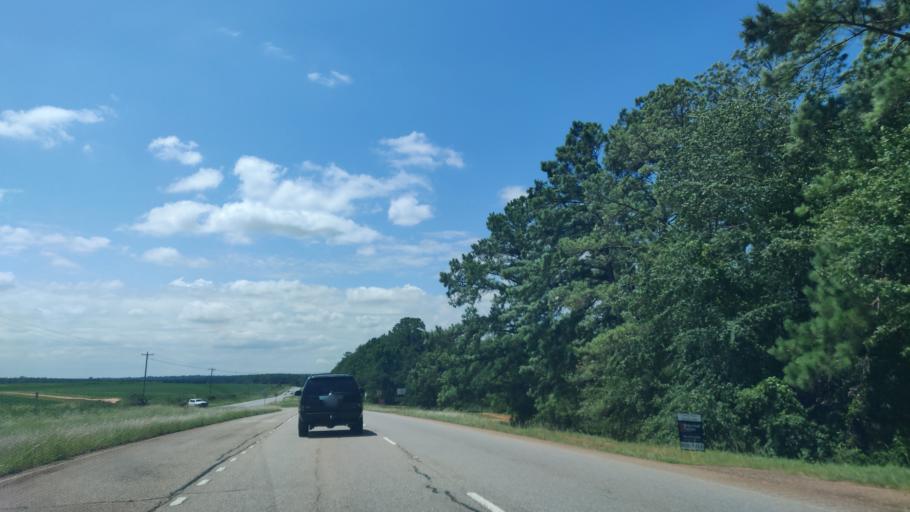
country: US
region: Georgia
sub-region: Stewart County
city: Richland
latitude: 32.0616
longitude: -84.6715
